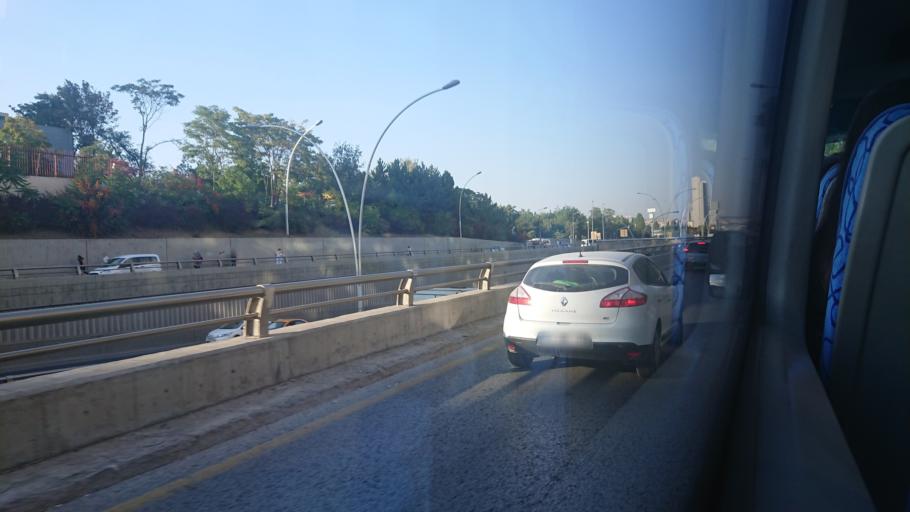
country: TR
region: Ankara
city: Ankara
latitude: 39.9301
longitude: 32.8187
